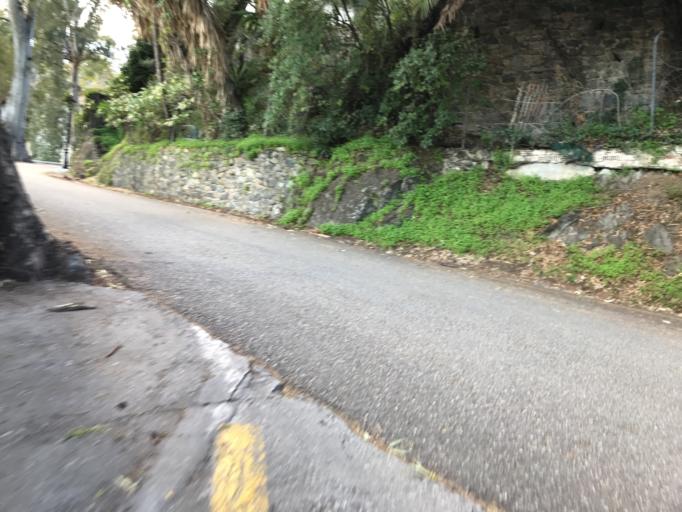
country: ES
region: Andalusia
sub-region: Provincia de Malaga
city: Tolox
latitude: 36.6829
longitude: -4.9070
